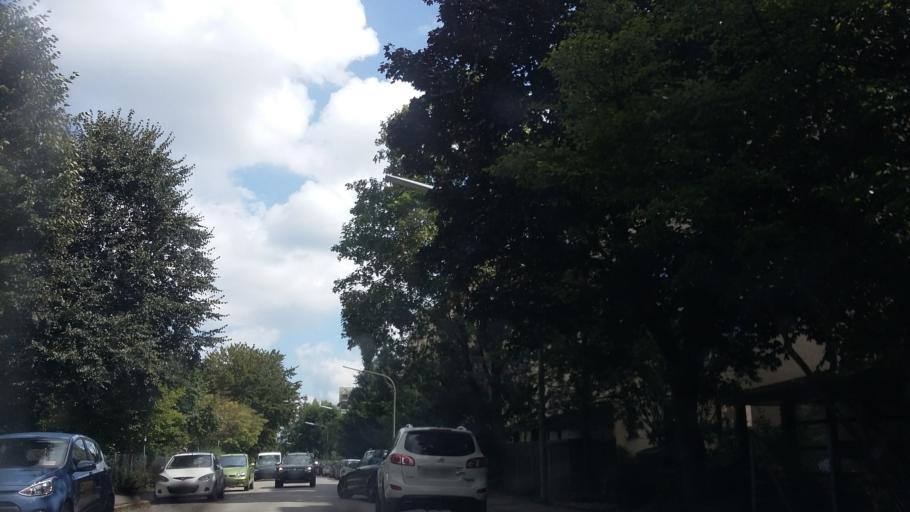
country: DE
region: Bavaria
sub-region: Swabia
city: Augsburg
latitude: 48.3395
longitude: 10.8782
